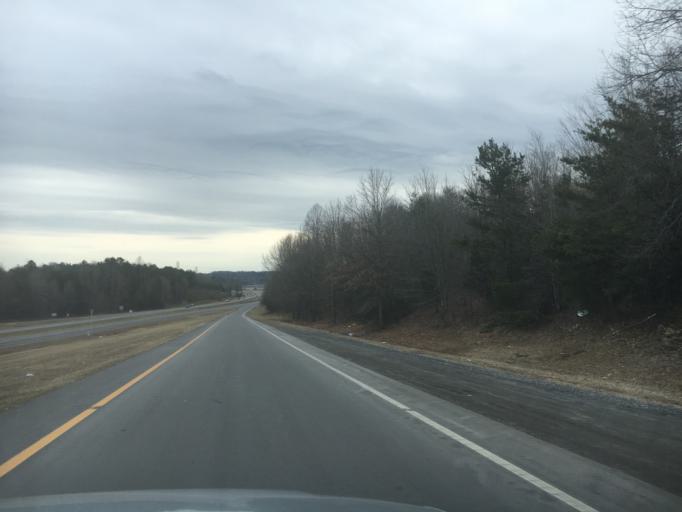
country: US
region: North Carolina
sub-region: Catawba County
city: Hickory
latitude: 35.7215
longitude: -81.3572
